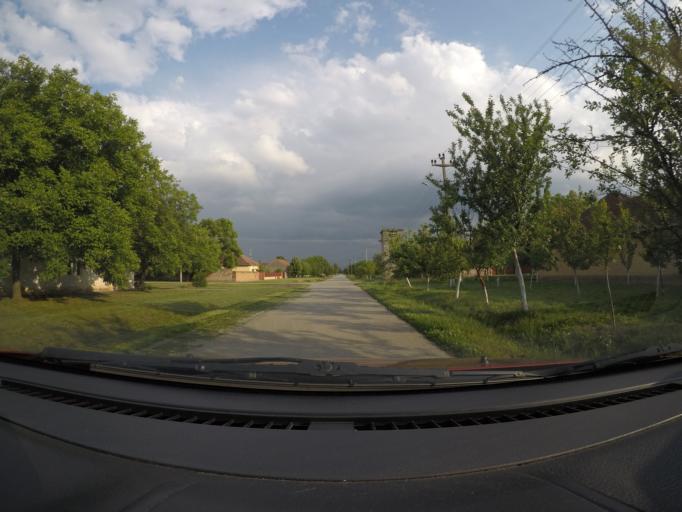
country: RS
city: Debeljaca
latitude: 45.0762
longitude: 20.5992
